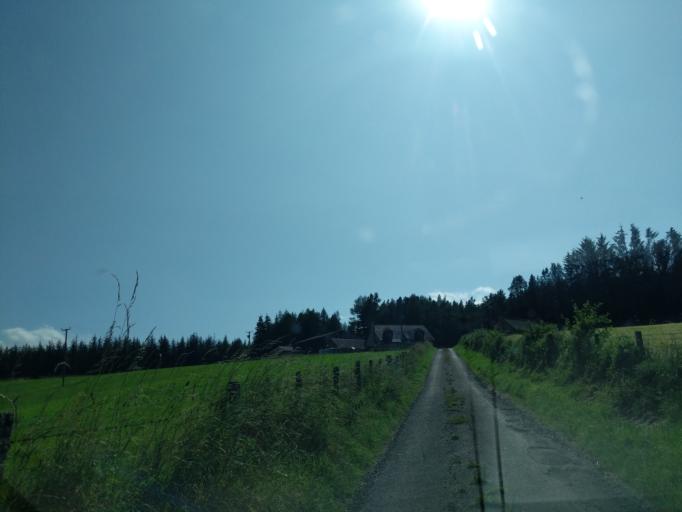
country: GB
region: Scotland
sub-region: Moray
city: Fochabers
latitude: 57.5890
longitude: -3.1102
